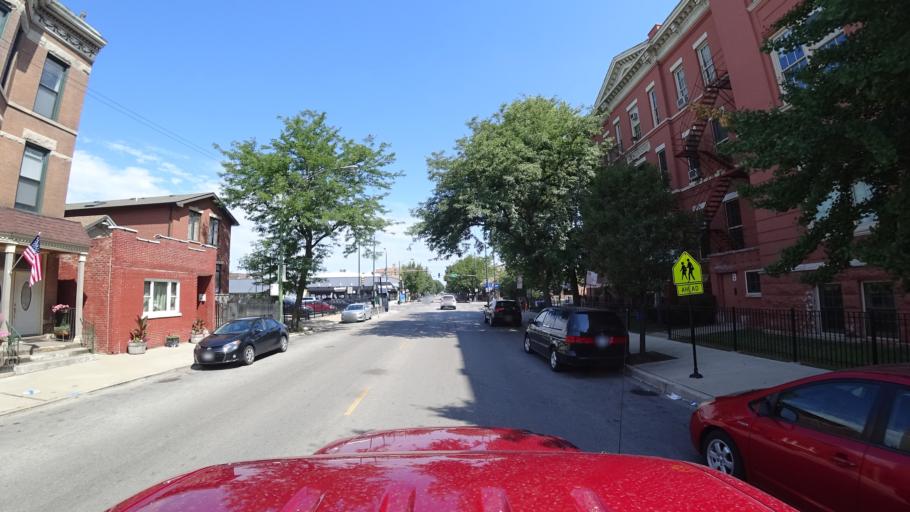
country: US
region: Illinois
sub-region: Cook County
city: Chicago
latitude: 41.8302
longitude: -87.6412
